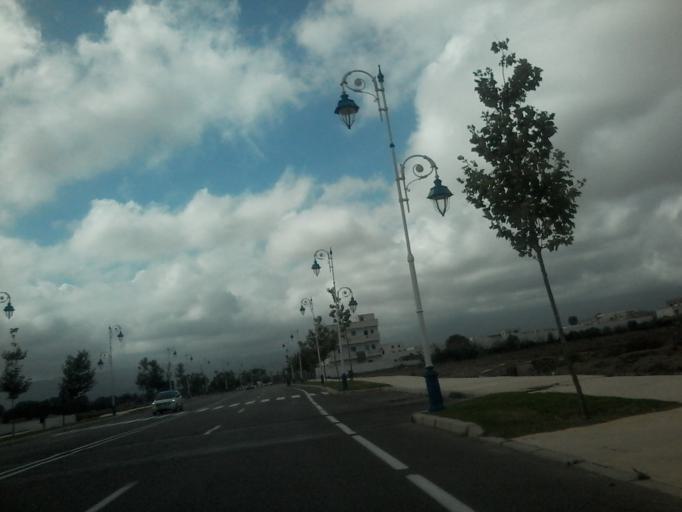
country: MA
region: Tanger-Tetouan
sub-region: Tetouan
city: Martil
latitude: 35.6522
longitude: -5.3068
